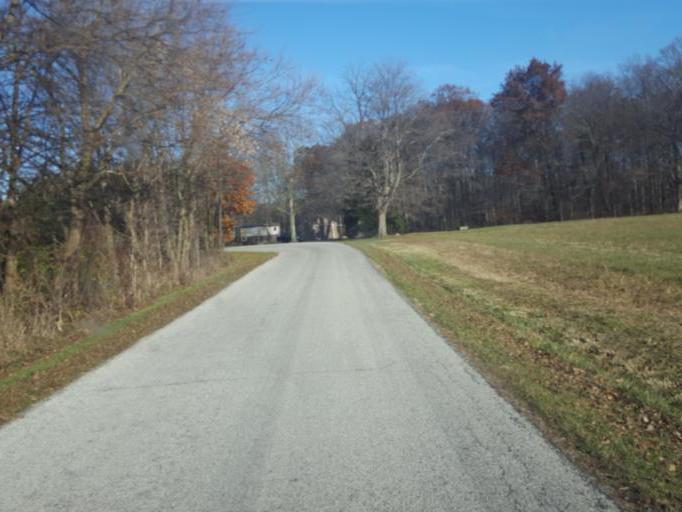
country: US
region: Ohio
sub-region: Crawford County
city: Bucyrus
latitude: 40.8305
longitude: -82.8968
